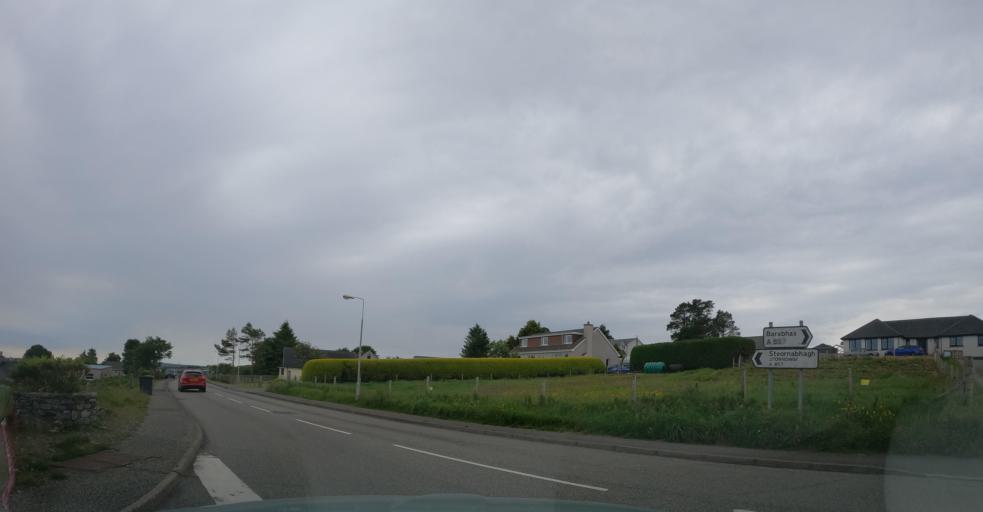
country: GB
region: Scotland
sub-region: Eilean Siar
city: Isle of Lewis
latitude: 58.2335
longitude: -6.3902
